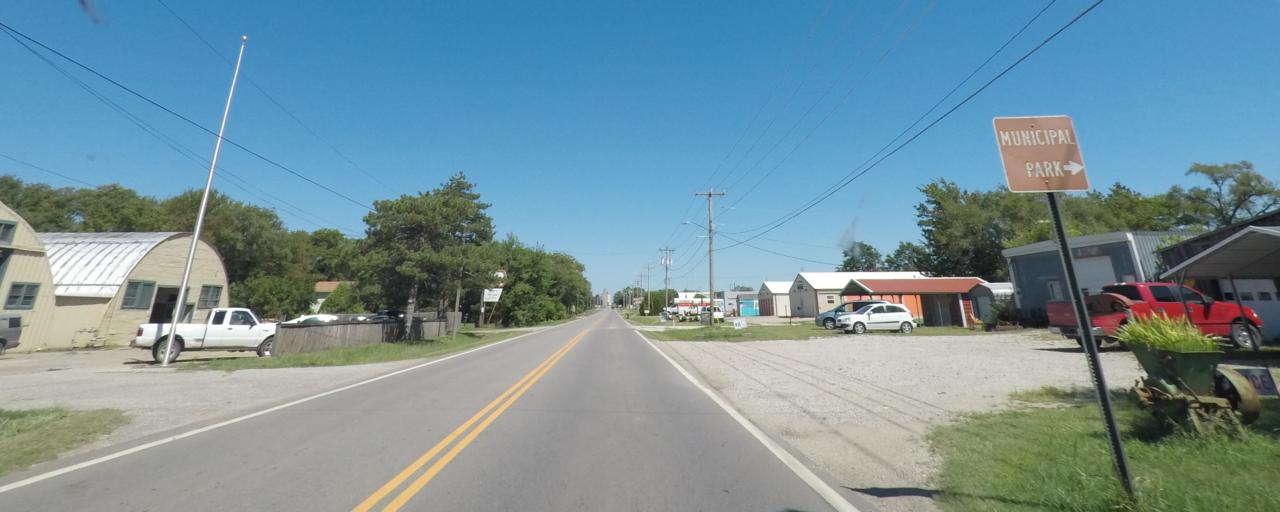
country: US
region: Kansas
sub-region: Sumner County
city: Wellington
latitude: 37.2845
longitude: -97.3943
